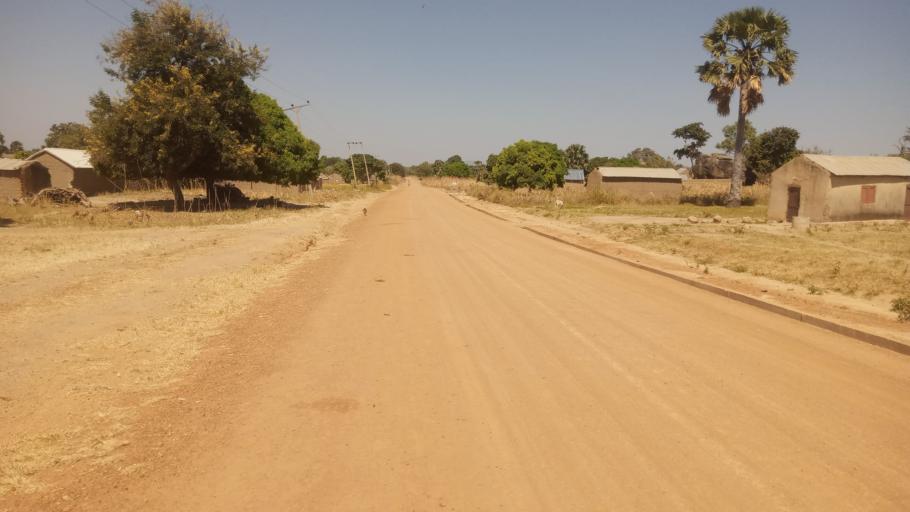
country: NG
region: Adamawa
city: Little Gombi
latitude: 10.2559
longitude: 12.9453
